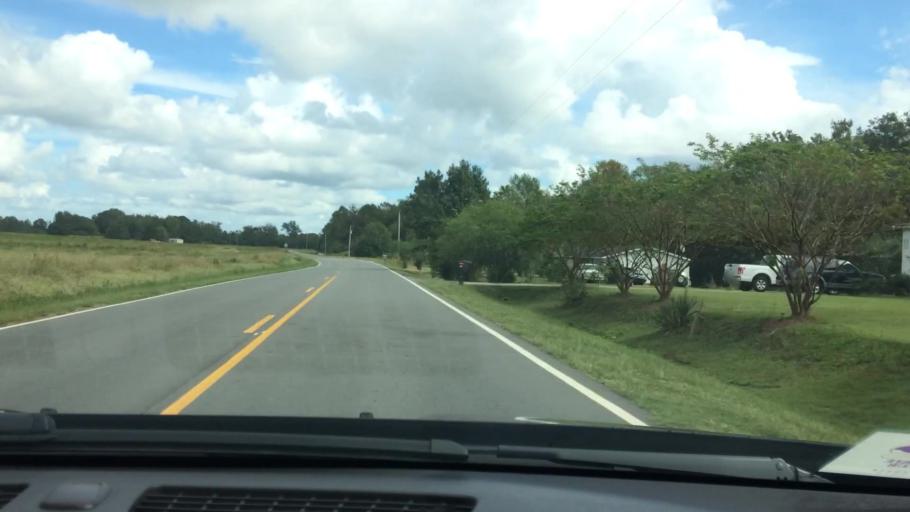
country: US
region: North Carolina
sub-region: Pitt County
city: Ayden
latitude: 35.4565
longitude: -77.4755
